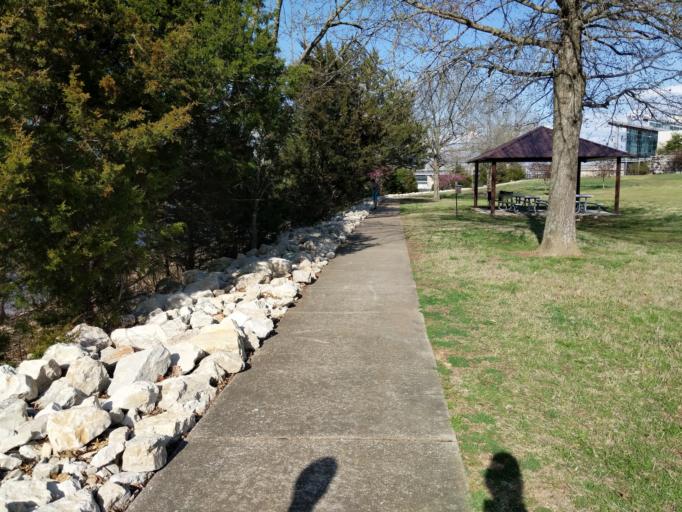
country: US
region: Missouri
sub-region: Taney County
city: Hollister
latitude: 36.5939
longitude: -93.3140
